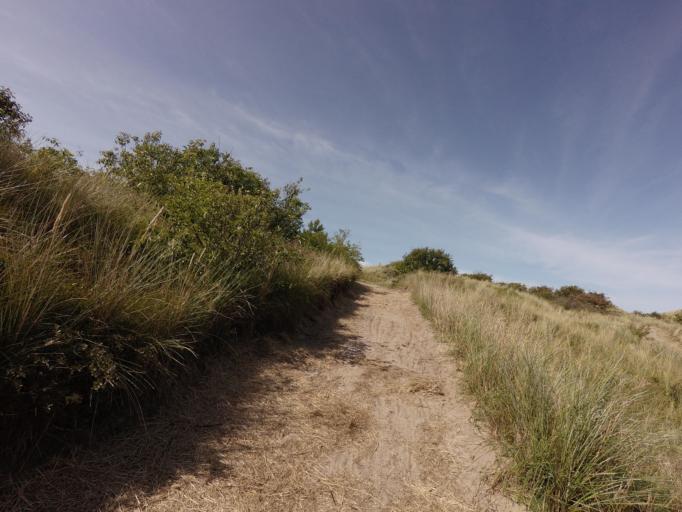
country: NL
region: Friesland
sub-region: Gemeente Ameland
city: Nes
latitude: 53.4551
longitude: 5.7687
